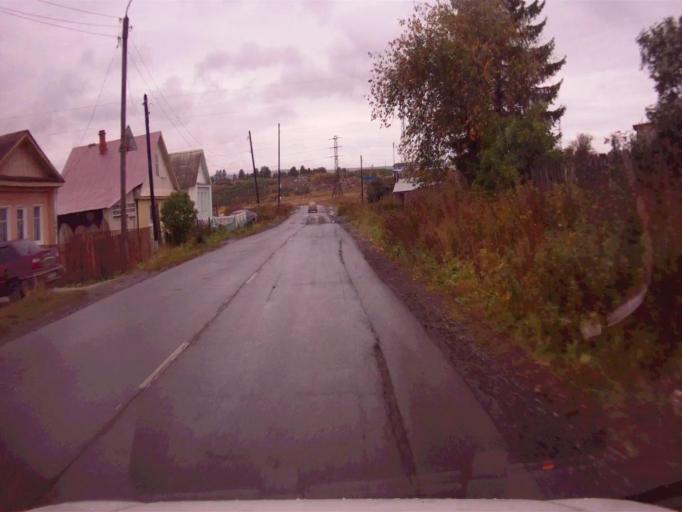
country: RU
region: Chelyabinsk
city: Verkhniy Ufaley
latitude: 56.0601
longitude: 60.2005
